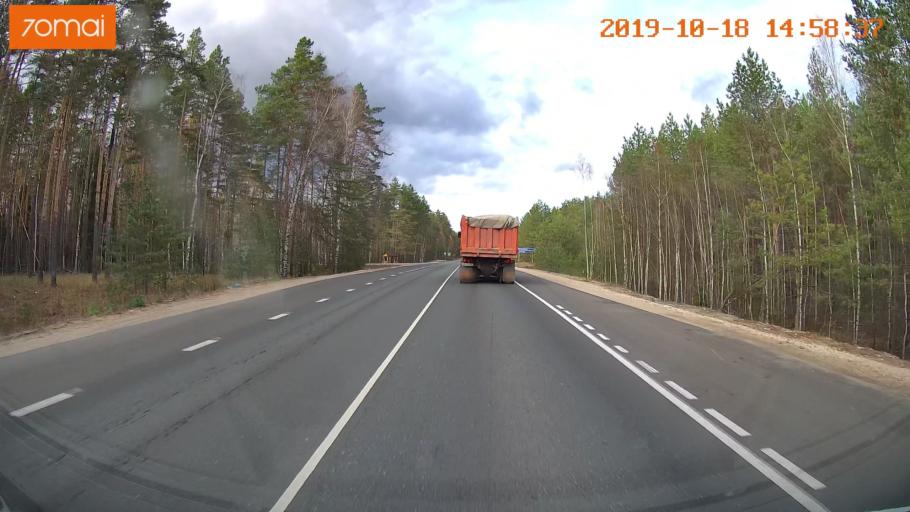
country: RU
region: Vladimir
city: Kurlovo
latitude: 55.4923
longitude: 40.5764
